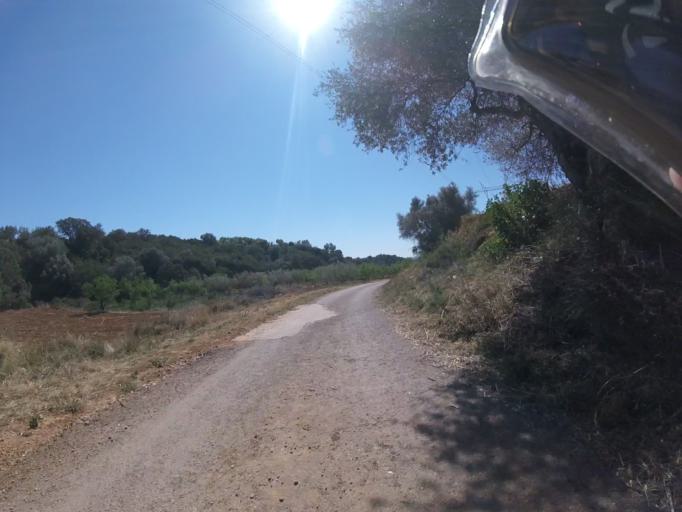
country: ES
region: Valencia
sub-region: Provincia de Castello
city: Cuevas de Vinroma
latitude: 40.3726
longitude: 0.1346
